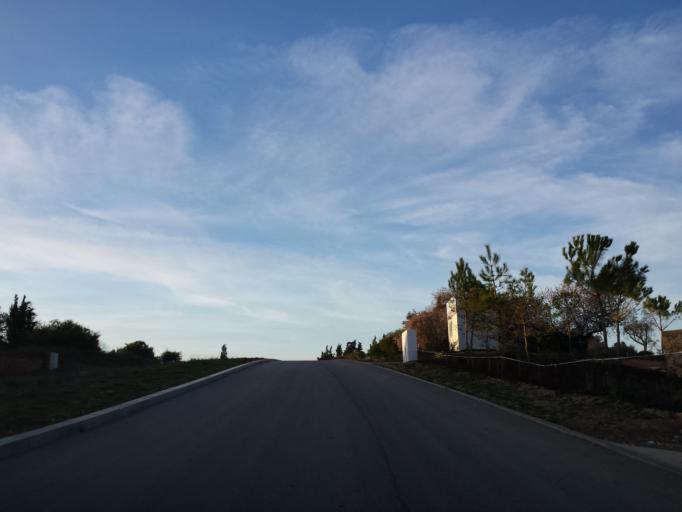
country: PT
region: Faro
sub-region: Lagos
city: Lagos
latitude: 37.1292
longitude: -8.6419
